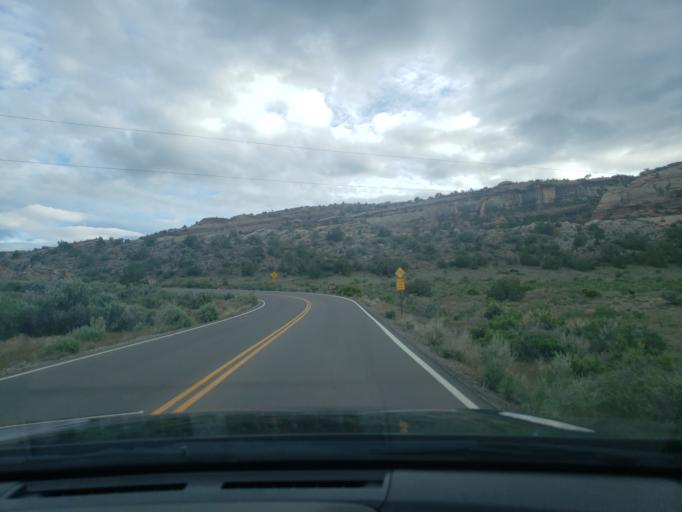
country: US
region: Colorado
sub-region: Mesa County
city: Redlands
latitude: 39.0344
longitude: -108.6315
